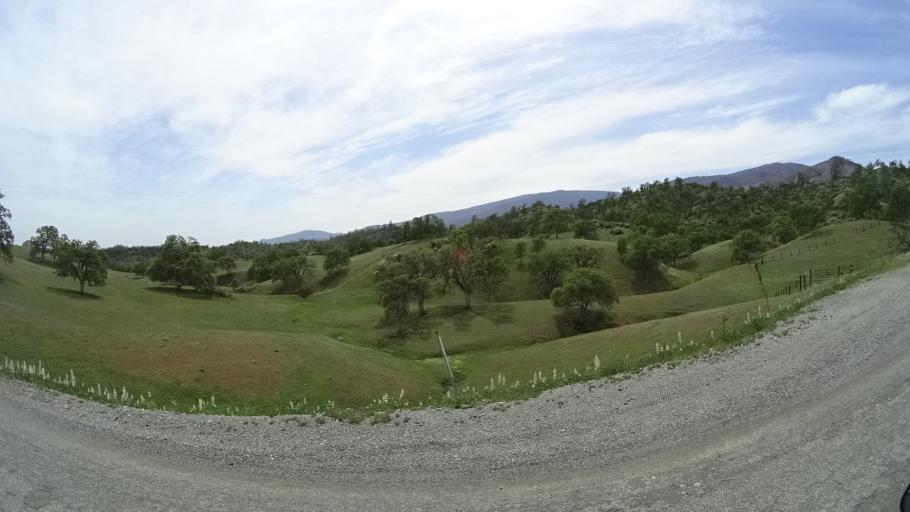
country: US
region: California
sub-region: Glenn County
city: Willows
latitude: 39.6171
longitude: -122.5907
